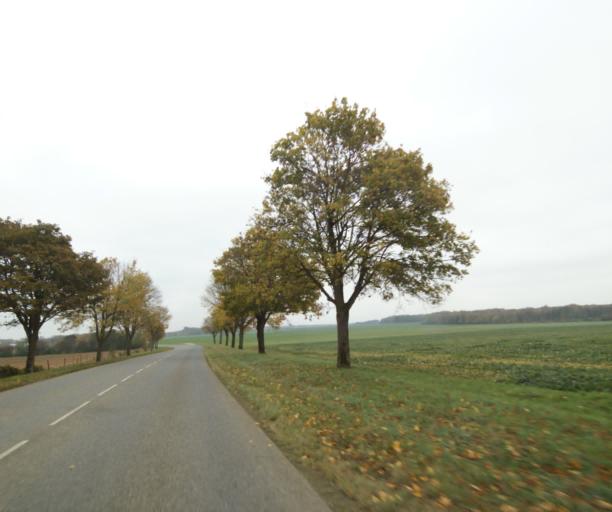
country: FR
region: Lorraine
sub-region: Departement de Meurthe-et-Moselle
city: Moutiers
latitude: 49.2494
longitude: 5.9597
